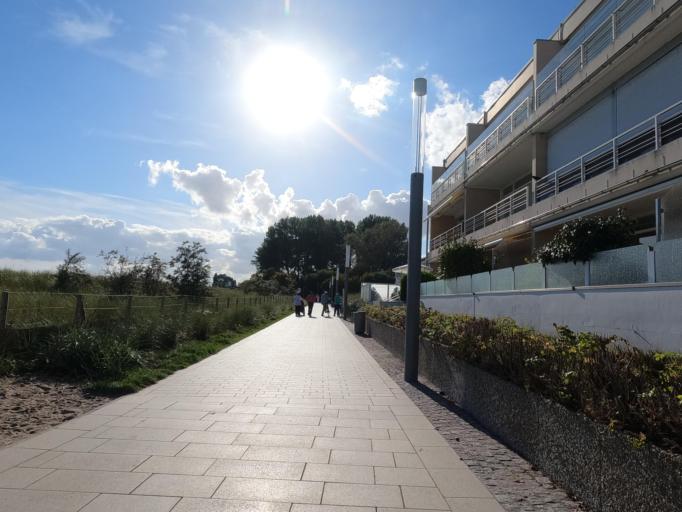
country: DE
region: Schleswig-Holstein
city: Grossenbrode
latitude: 54.3574
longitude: 11.0873
